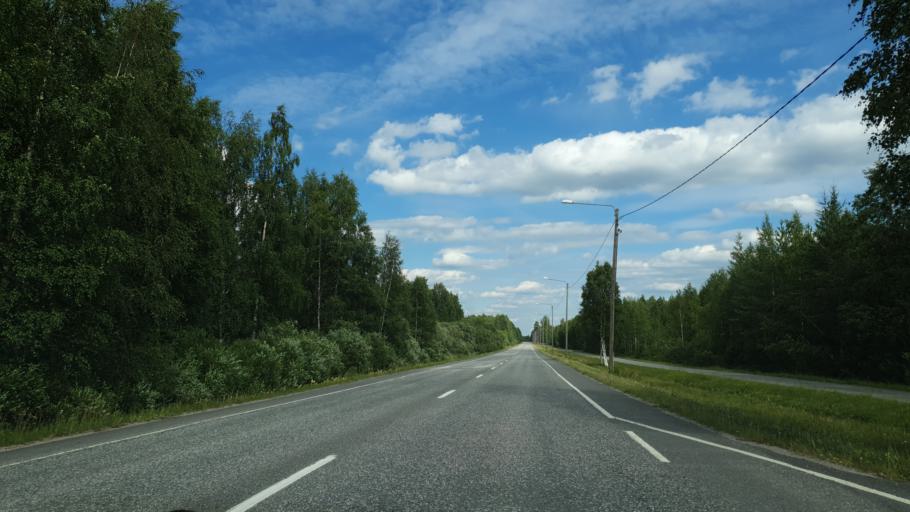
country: FI
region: Kainuu
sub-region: Kajaani
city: Kajaani
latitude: 64.2519
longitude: 27.7898
